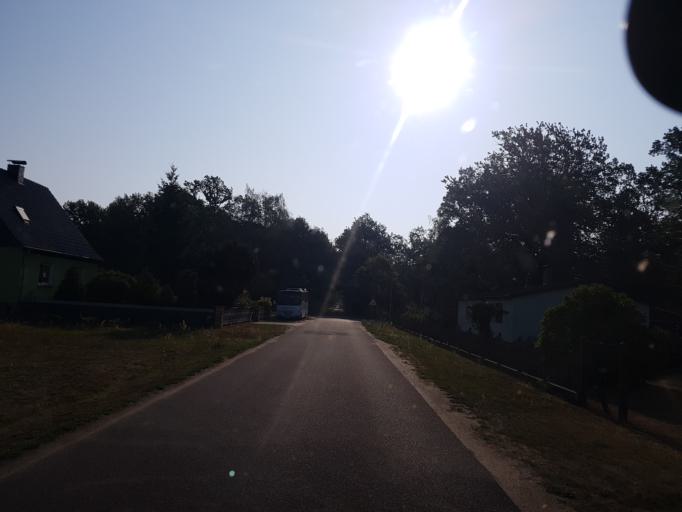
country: DE
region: Brandenburg
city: Sonnewalde
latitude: 51.6879
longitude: 13.6893
